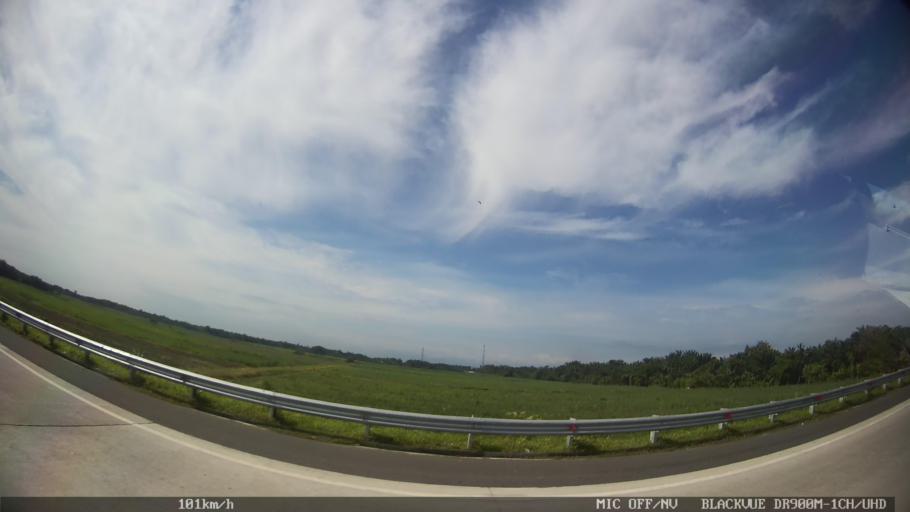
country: ID
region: North Sumatra
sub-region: Kabupaten Langkat
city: Stabat
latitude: 3.7127
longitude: 98.5270
